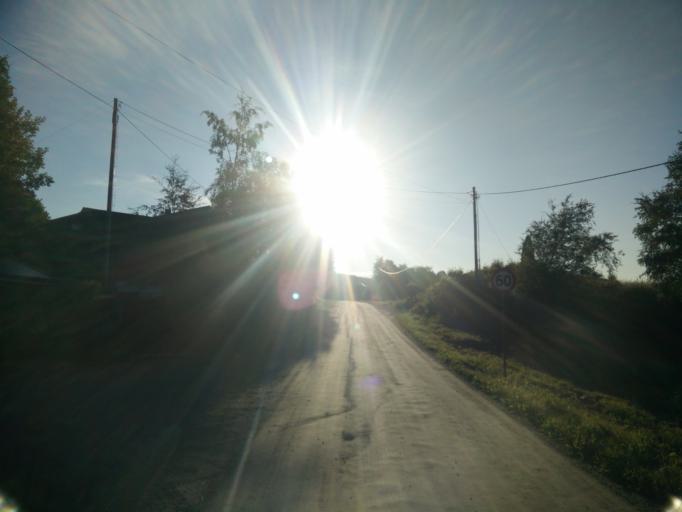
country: NO
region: Sor-Trondelag
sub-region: Skaun
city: Borsa
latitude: 63.3367
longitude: 10.0456
